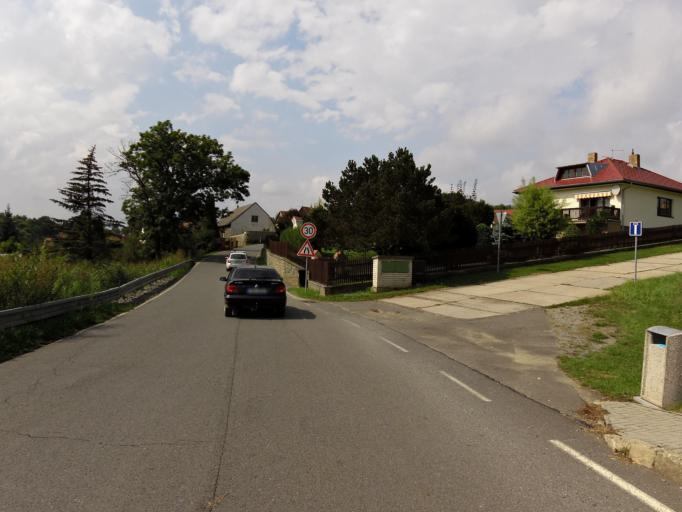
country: CZ
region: Central Bohemia
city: Tynec nad Sazavou
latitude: 49.8545
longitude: 14.5587
